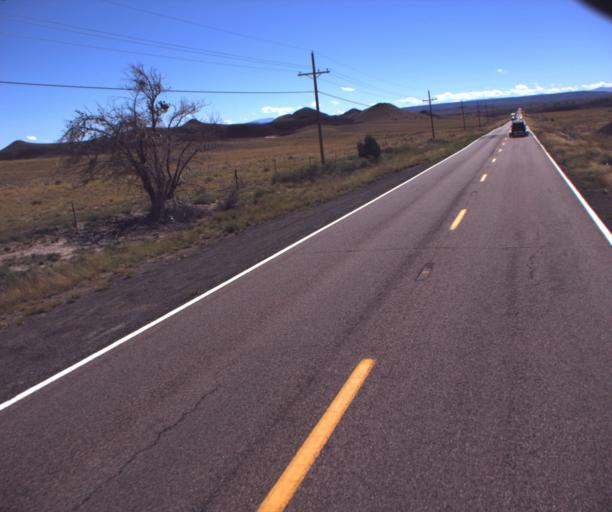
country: US
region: Arizona
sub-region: Apache County
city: Saint Johns
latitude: 34.5539
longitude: -109.3430
